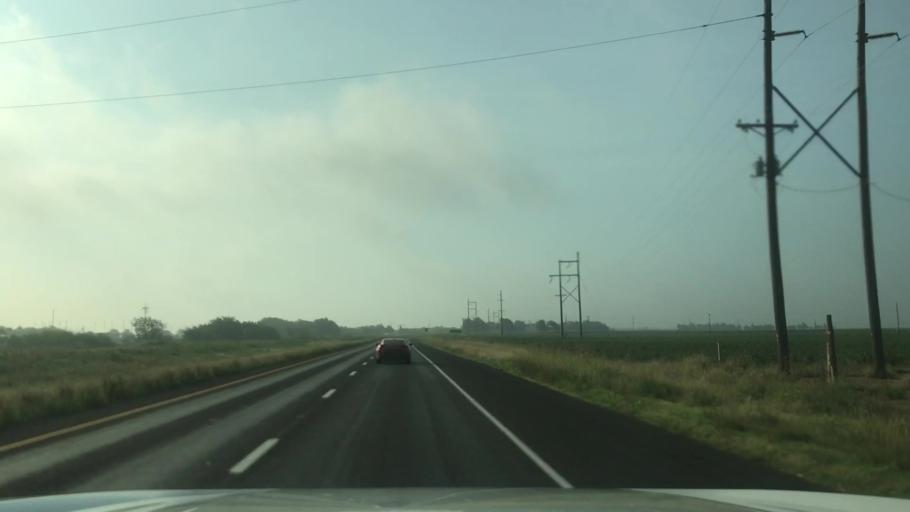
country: US
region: Texas
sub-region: Lubbock County
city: Slaton
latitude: 33.3632
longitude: -101.5614
